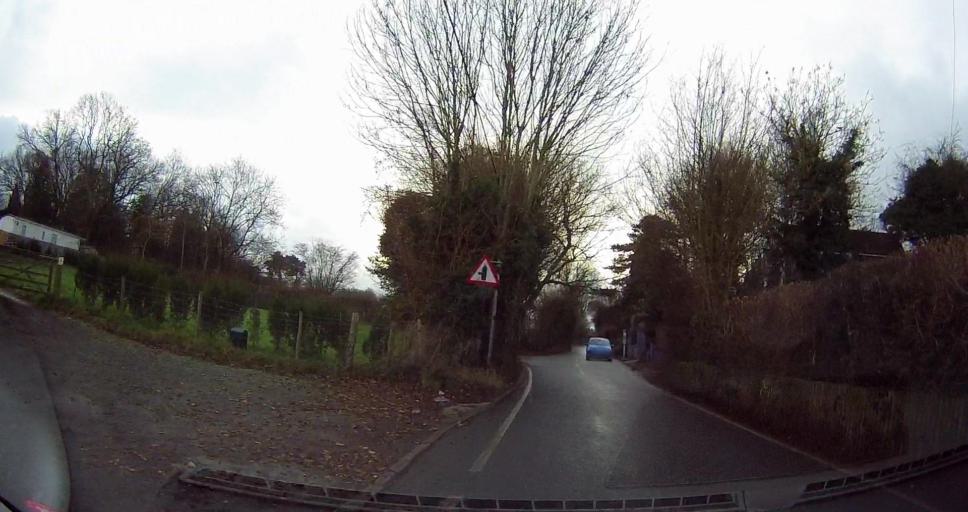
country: GB
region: England
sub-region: Greater London
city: Orpington
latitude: 51.3371
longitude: 0.0784
